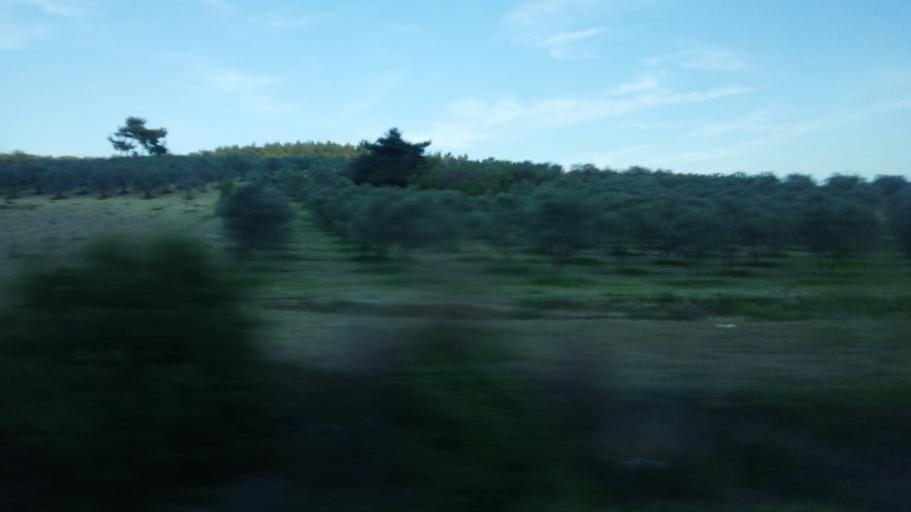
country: TR
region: Manisa
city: Gelembe
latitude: 39.2122
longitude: 27.8603
